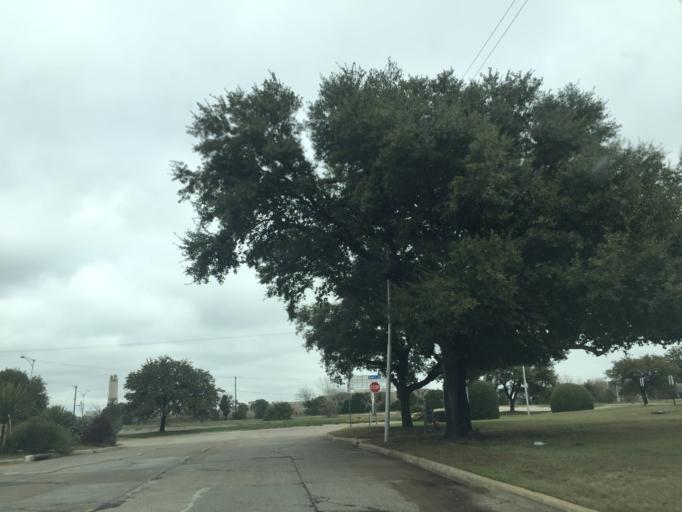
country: US
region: Texas
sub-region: Tarrant County
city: Arlington
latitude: 32.7560
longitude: -97.0600
